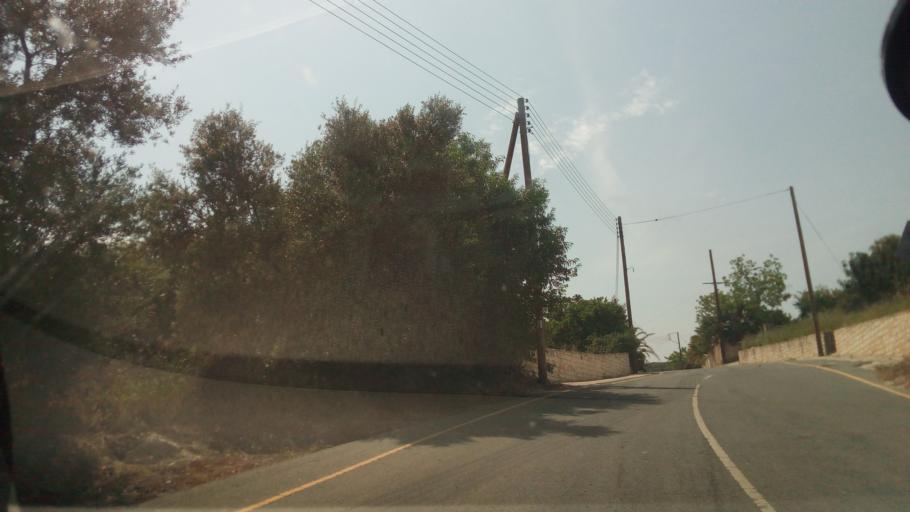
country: CY
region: Pafos
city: Polis
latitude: 34.9550
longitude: 32.4509
